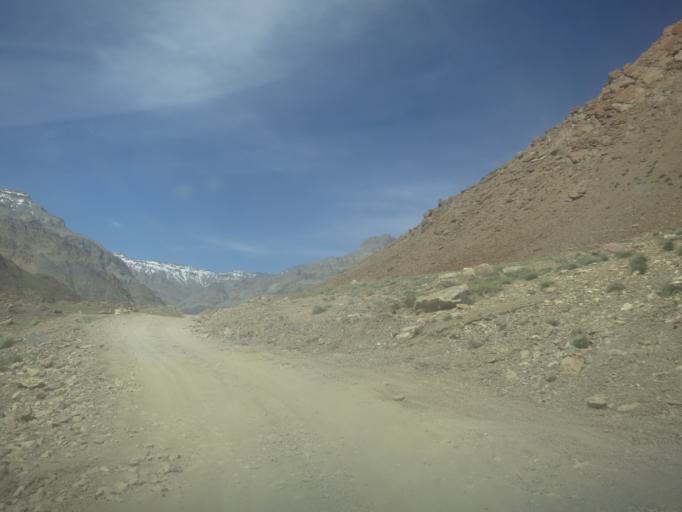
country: IN
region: Himachal Pradesh
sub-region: Kulu
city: Manali
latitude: 32.4343
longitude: 77.6771
